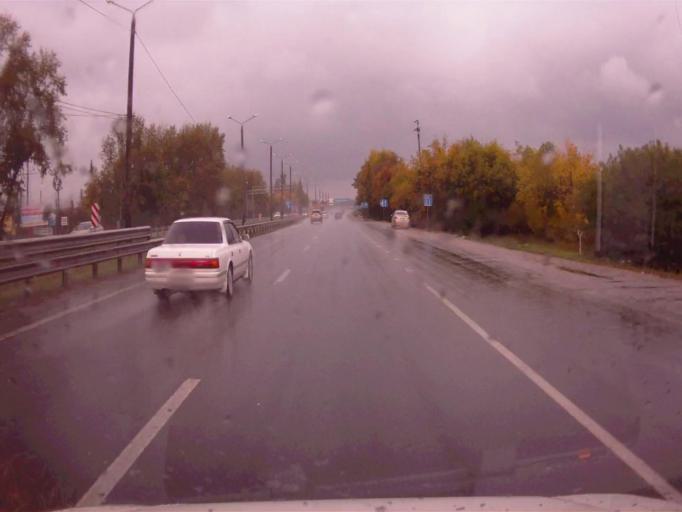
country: RU
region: Chelyabinsk
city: Dolgoderevenskoye
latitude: 55.2576
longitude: 61.3512
